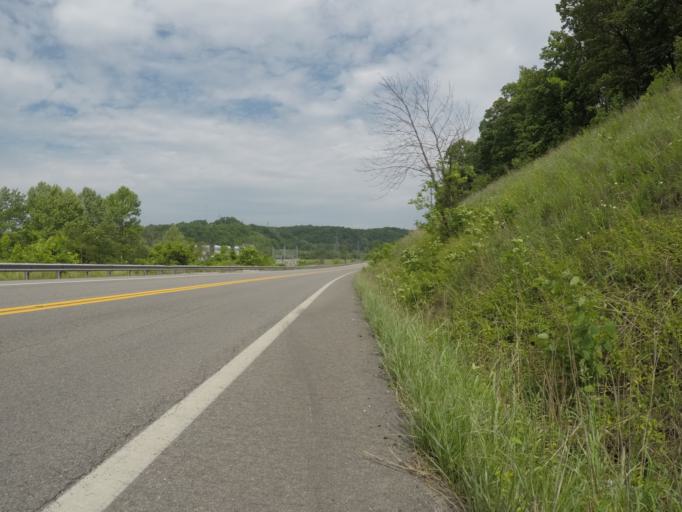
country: US
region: West Virginia
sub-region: Wayne County
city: Kenova
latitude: 38.3429
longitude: -82.5903
